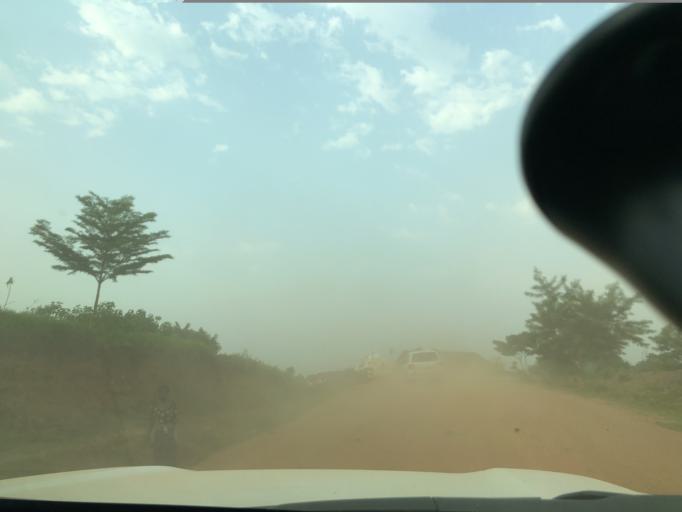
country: UG
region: Western Region
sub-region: Kasese District
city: Margherita
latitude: 0.3251
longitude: 29.6768
